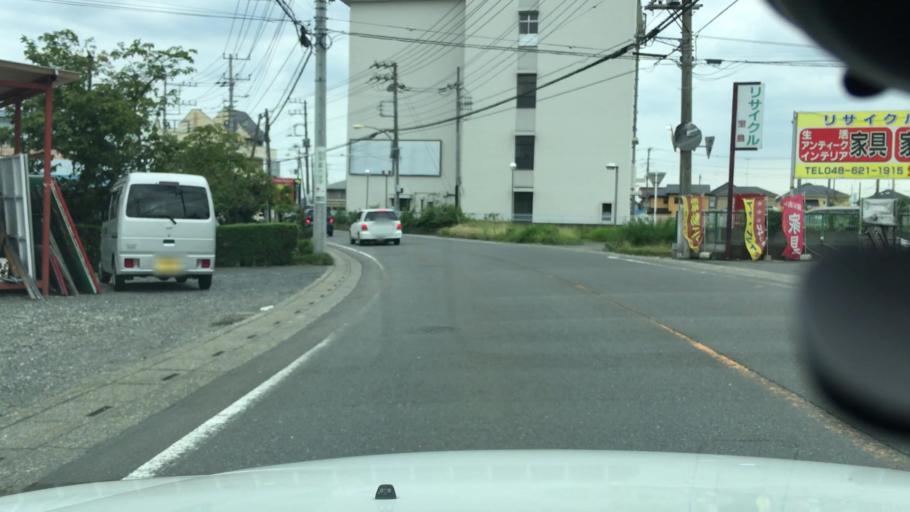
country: JP
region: Saitama
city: Yono
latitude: 35.9125
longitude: 139.5755
